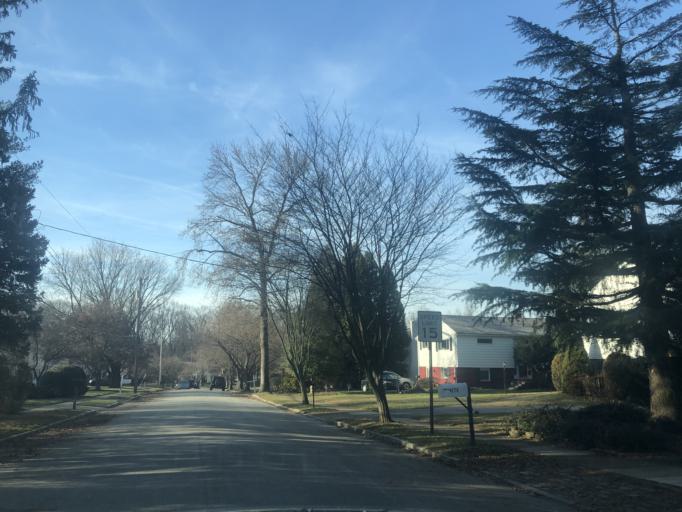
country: US
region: Pennsylvania
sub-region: Delaware County
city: Radnor
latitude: 40.0228
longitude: -75.3399
